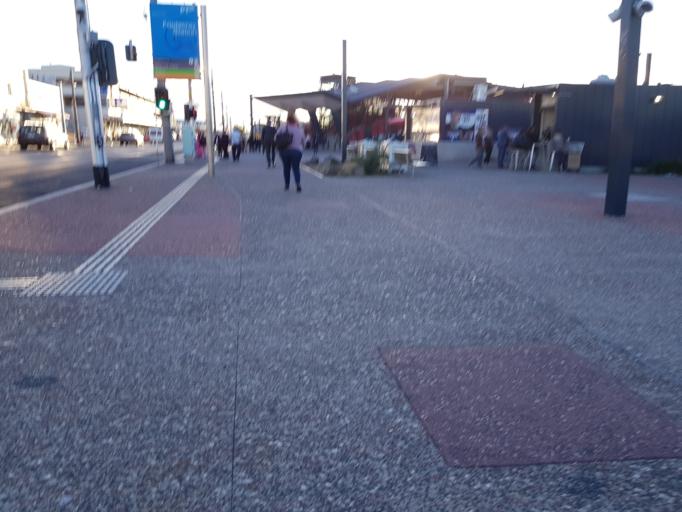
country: AU
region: Victoria
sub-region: Maribyrnong
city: Footscray
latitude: -37.8018
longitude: 144.9006
